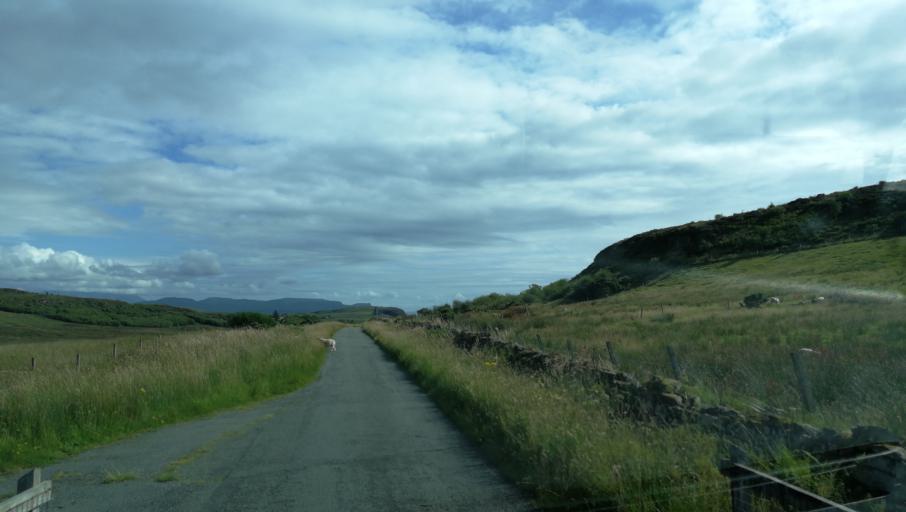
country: GB
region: Scotland
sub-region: Highland
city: Isle of Skye
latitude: 57.4040
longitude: -6.5686
